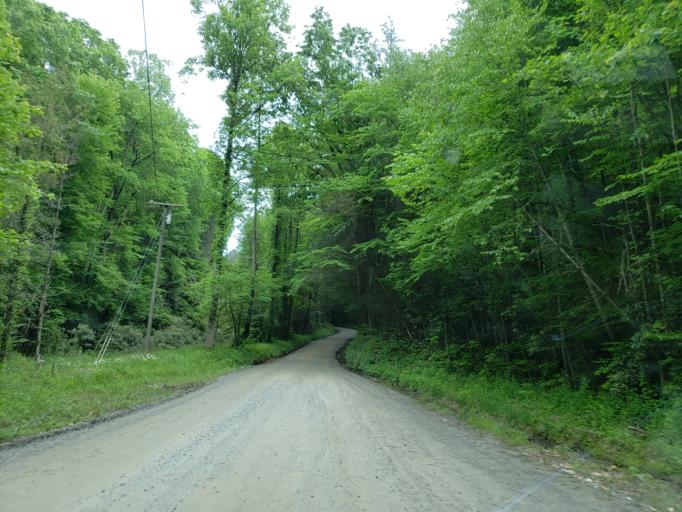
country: US
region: Georgia
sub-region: Fannin County
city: Blue Ridge
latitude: 34.8526
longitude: -84.4187
